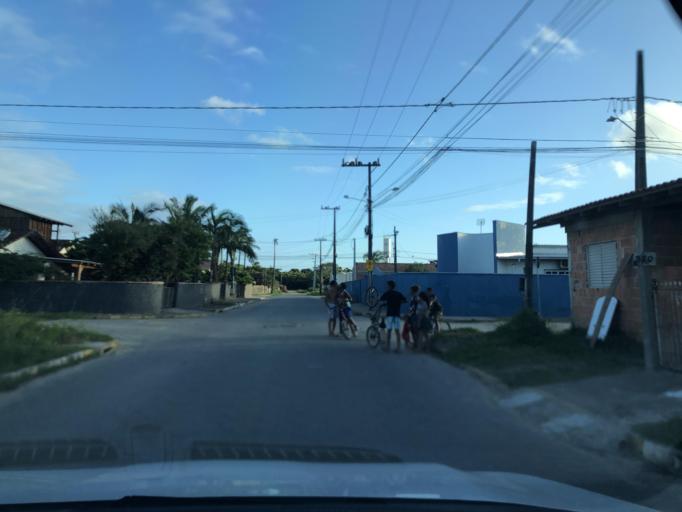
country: BR
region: Santa Catarina
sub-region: Sao Francisco Do Sul
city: Sao Francisco do Sul
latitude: -26.2344
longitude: -48.5237
